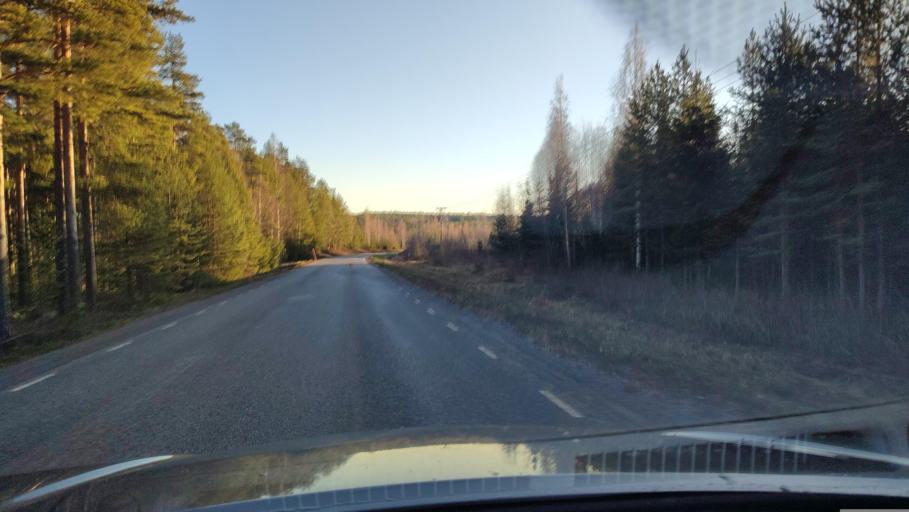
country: SE
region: Vaesterbotten
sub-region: Skelleftea Kommun
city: Viken
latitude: 64.6941
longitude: 20.9335
